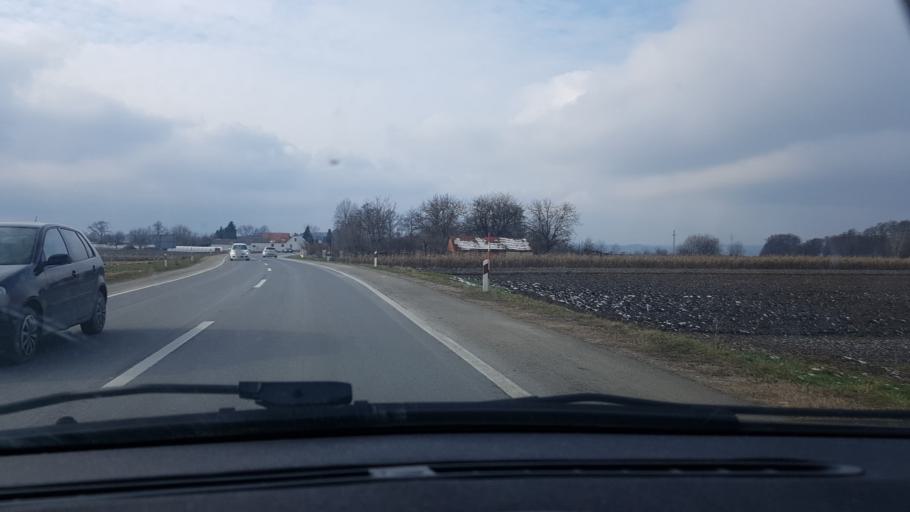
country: HR
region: Varazdinska
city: Tuzno
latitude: 46.2826
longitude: 16.2294
